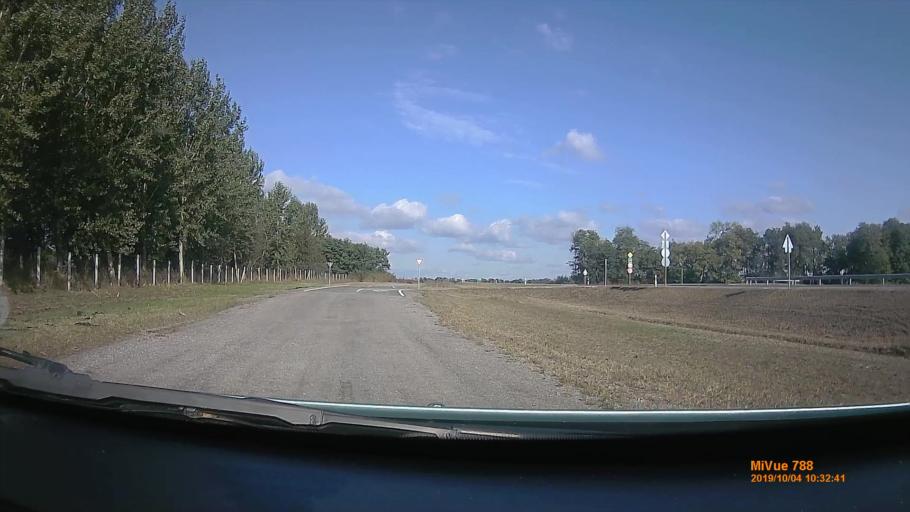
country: HU
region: Szabolcs-Szatmar-Bereg
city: Nyirtelek
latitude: 47.9658
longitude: 21.6580
